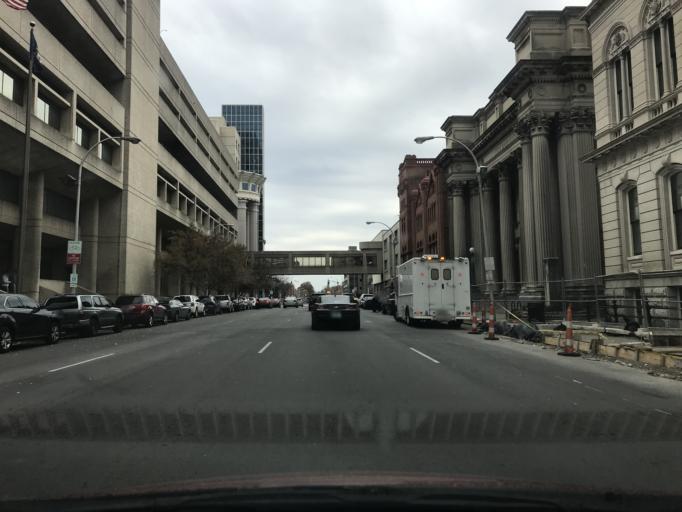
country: US
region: Kentucky
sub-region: Jefferson County
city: Louisville
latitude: 38.2543
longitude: -85.7605
